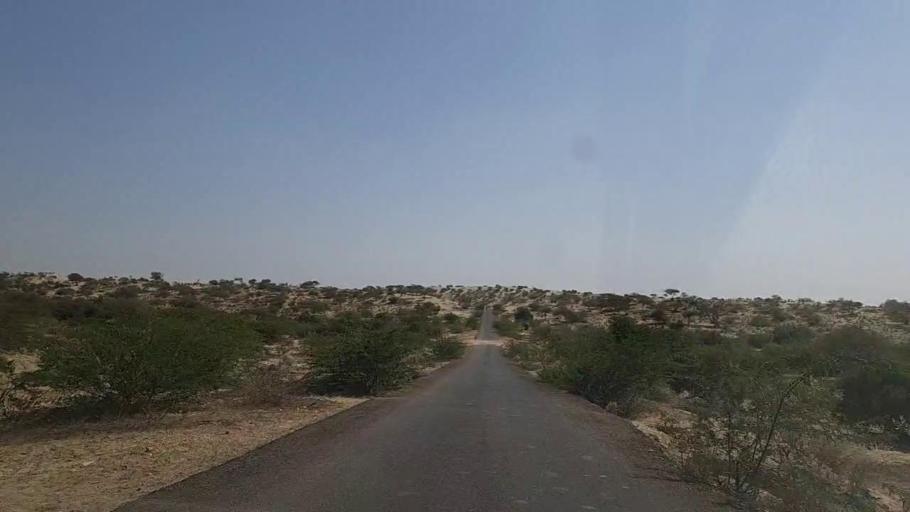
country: PK
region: Sindh
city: Diplo
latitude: 24.4866
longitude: 69.4471
